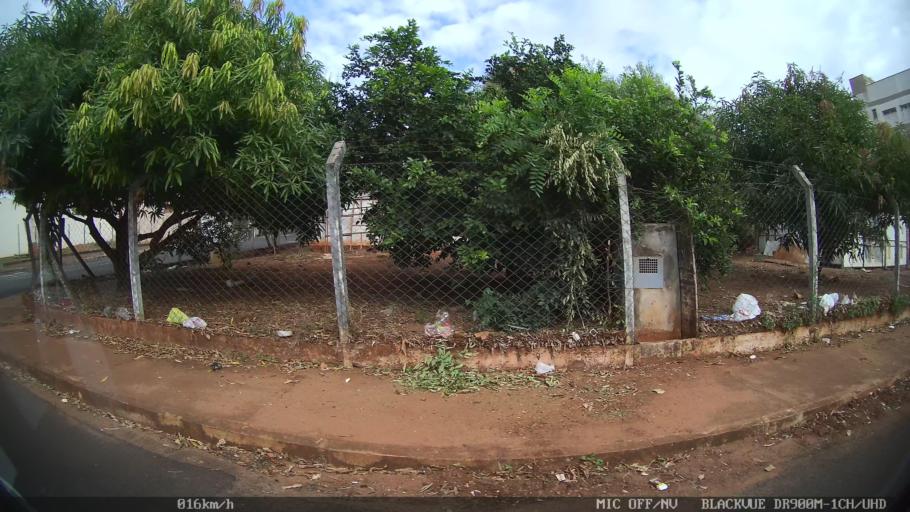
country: BR
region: Sao Paulo
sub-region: Sao Jose Do Rio Preto
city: Sao Jose do Rio Preto
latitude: -20.8175
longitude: -49.3503
